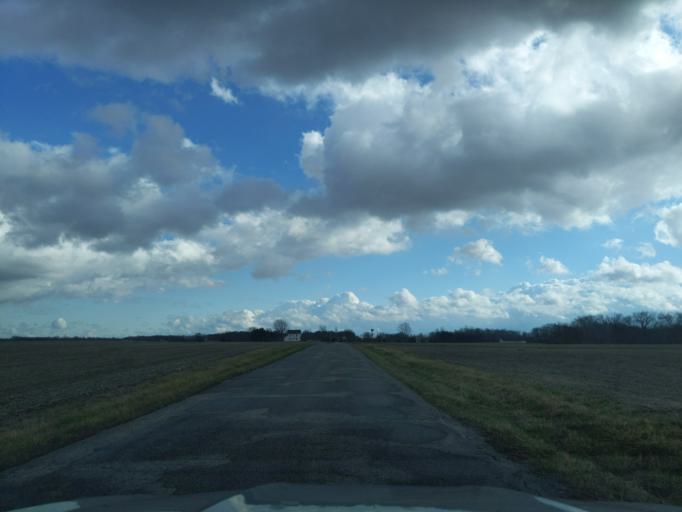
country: US
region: Indiana
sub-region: Decatur County
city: Greensburg
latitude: 39.4093
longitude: -85.5278
